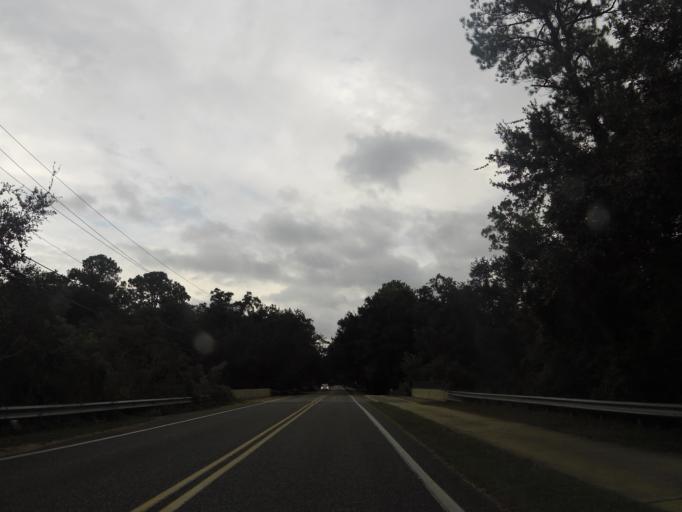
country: US
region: Alabama
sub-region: Baldwin County
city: Point Clear
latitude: 30.4609
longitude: -87.9166
